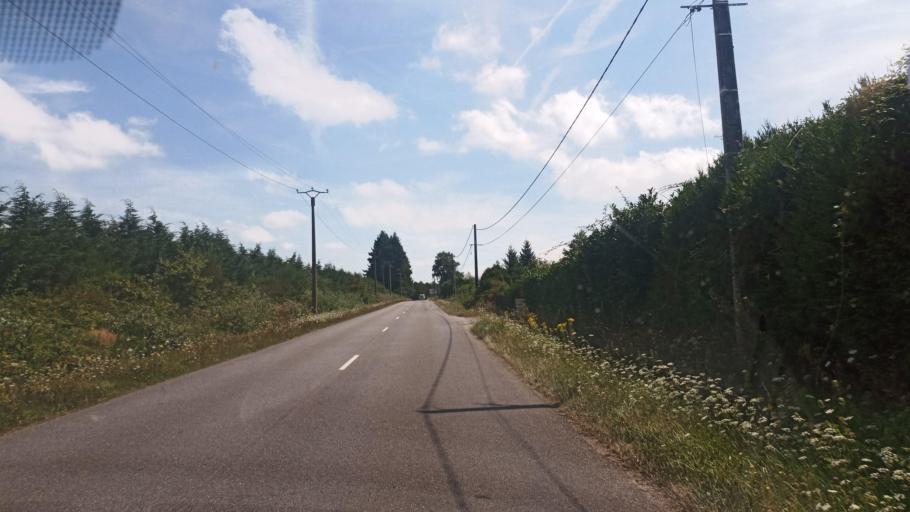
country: FR
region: Limousin
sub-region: Departement de la Haute-Vienne
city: Veyrac
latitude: 45.9021
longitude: 1.0816
